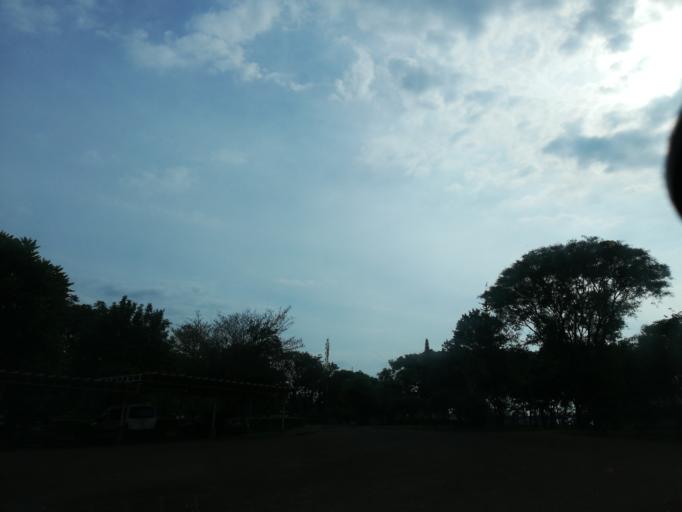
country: AR
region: Misiones
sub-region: Departamento de Capital
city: Posadas
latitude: -27.4353
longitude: -55.8880
